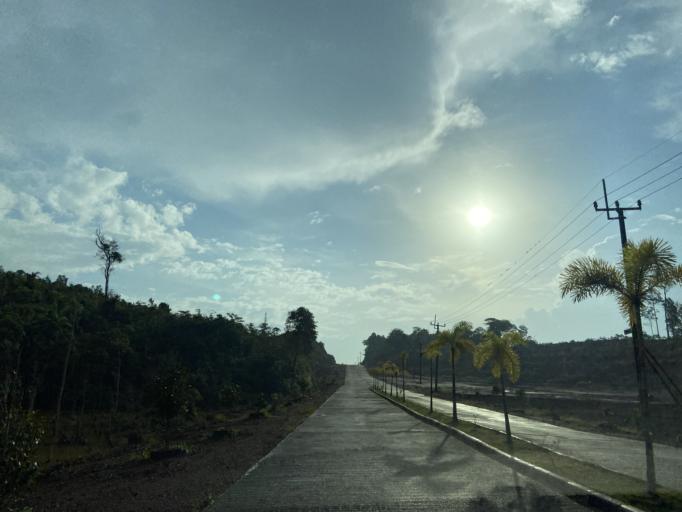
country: ID
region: Riau Islands
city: Tanjungpinang
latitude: 0.8959
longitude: 104.1254
